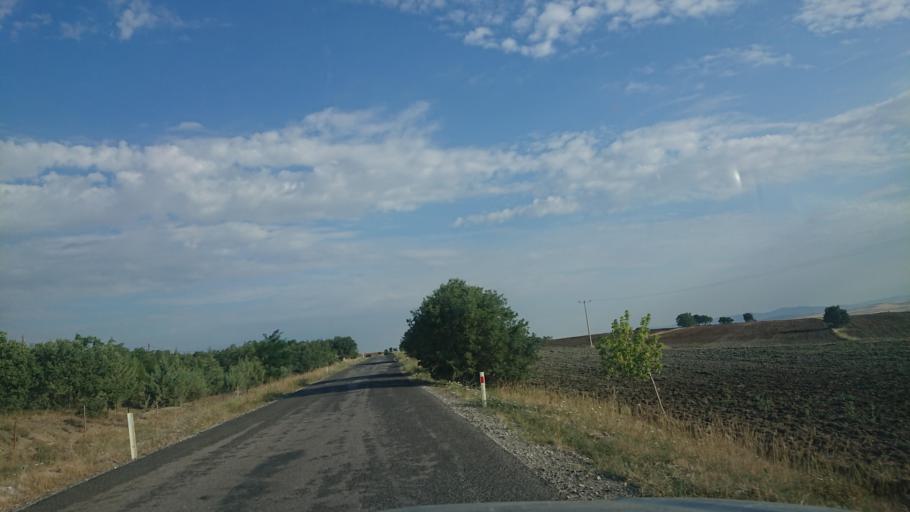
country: TR
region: Aksaray
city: Ortakoy
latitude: 38.8063
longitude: 34.0602
